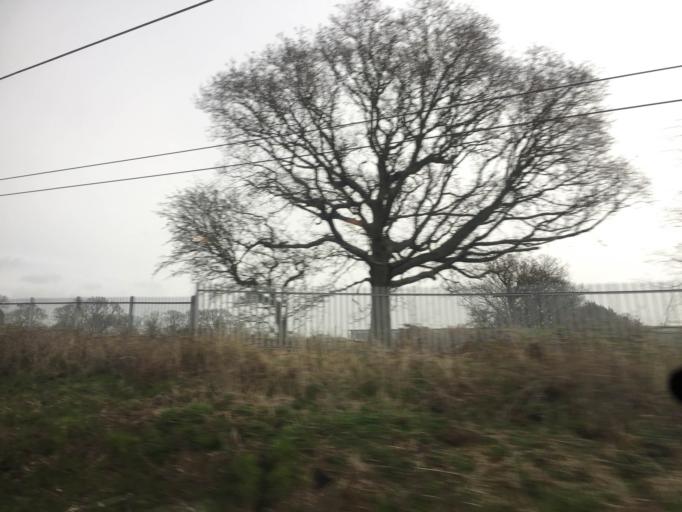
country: GB
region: England
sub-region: Lancashire
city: Euxton
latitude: 53.6827
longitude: -2.6795
